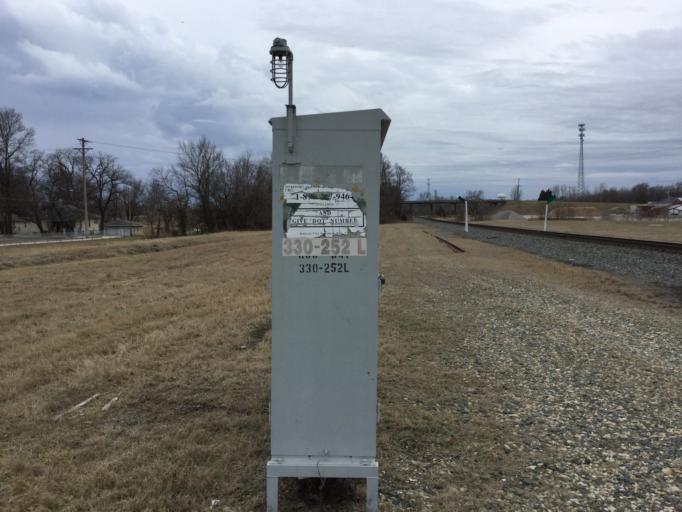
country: US
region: Kansas
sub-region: Crawford County
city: Pittsburg
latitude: 37.4254
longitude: -94.6865
